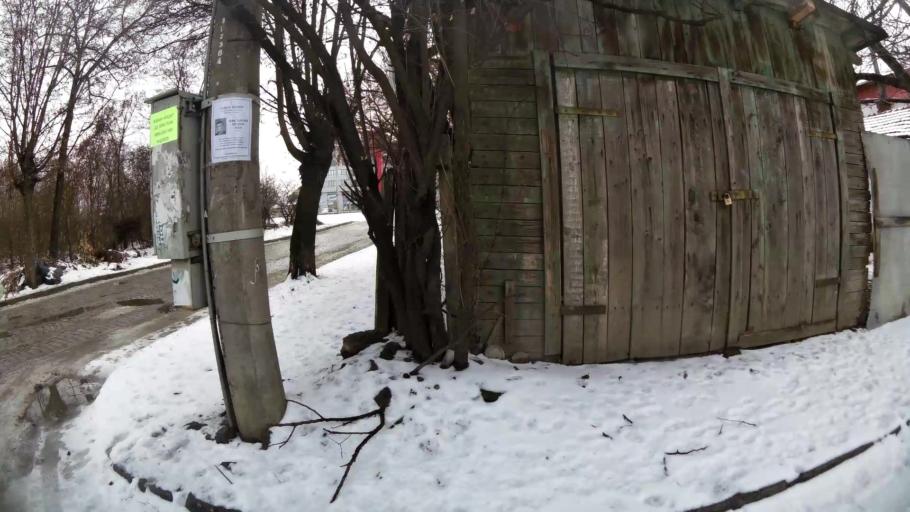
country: BG
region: Sofia-Capital
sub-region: Stolichna Obshtina
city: Sofia
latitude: 42.7026
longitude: 23.3804
